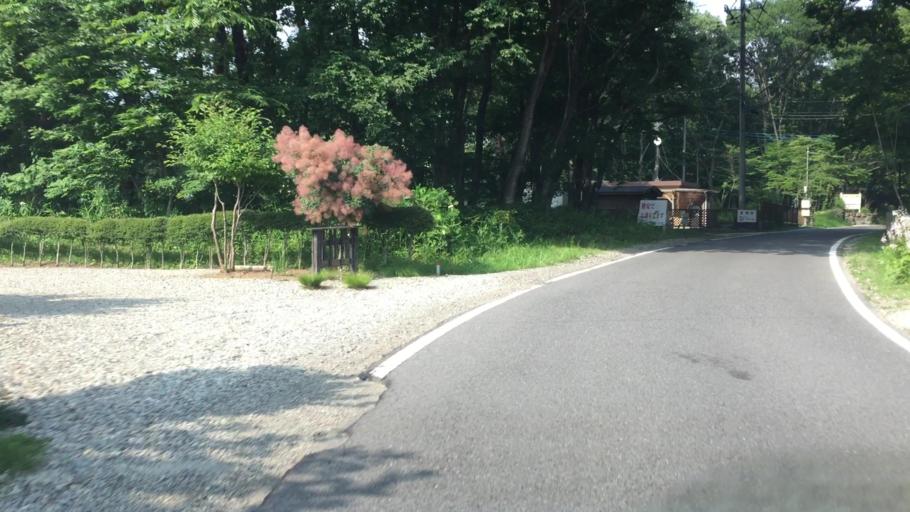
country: JP
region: Tochigi
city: Kuroiso
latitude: 37.0326
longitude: 140.0239
